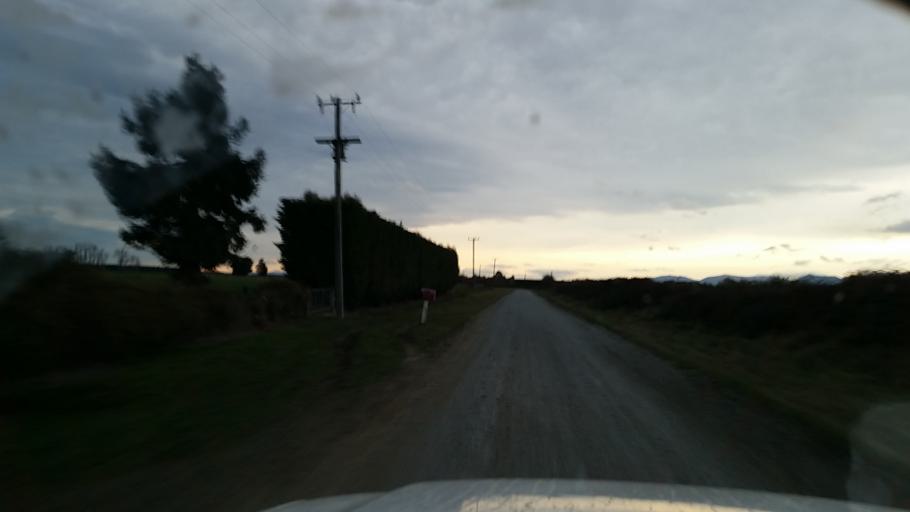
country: NZ
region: Canterbury
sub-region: Ashburton District
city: Ashburton
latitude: -43.8266
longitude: 171.6381
